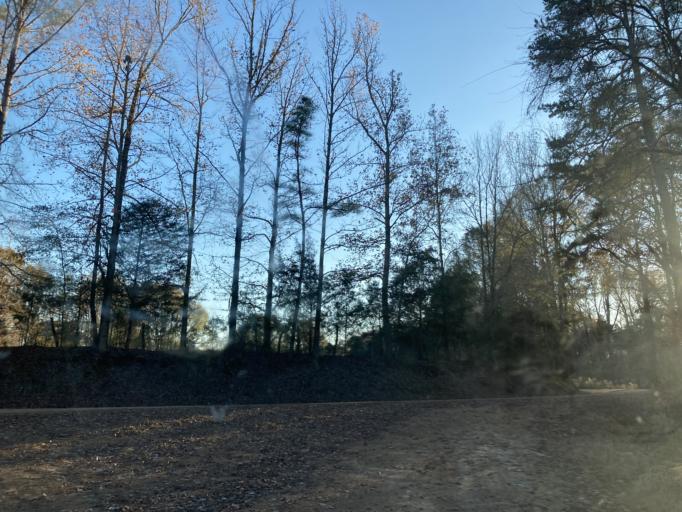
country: US
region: Mississippi
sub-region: Yazoo County
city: Yazoo City
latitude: 32.9463
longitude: -90.2848
